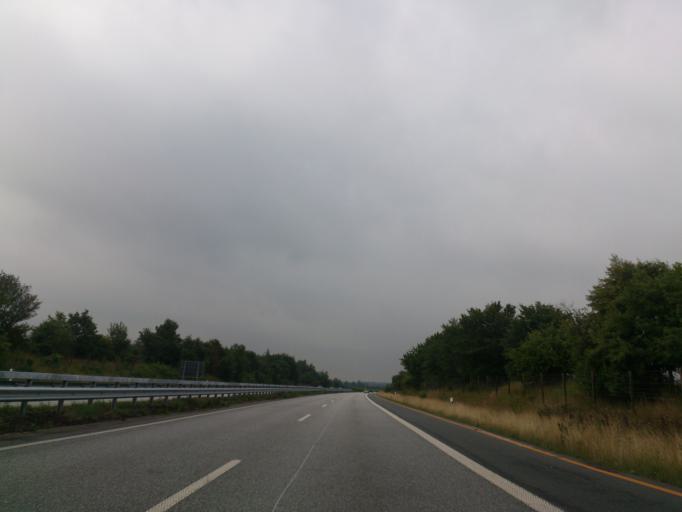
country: DE
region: Schleswig-Holstein
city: Tensbuttel-Rost
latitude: 54.0993
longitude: 9.2658
